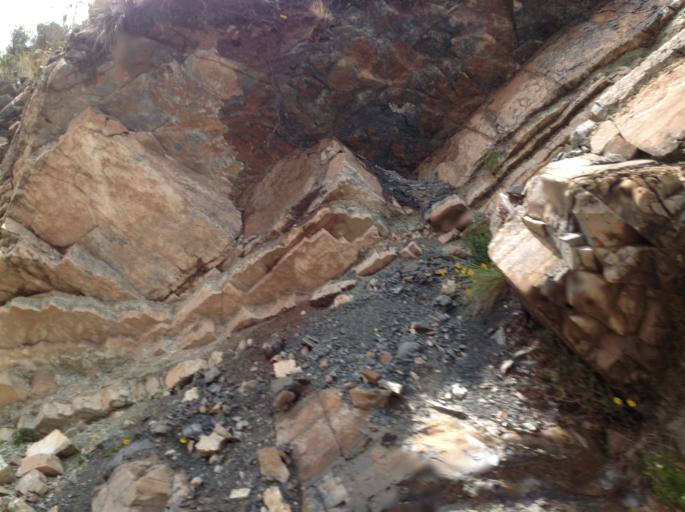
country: BO
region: La Paz
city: Yumani
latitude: -15.7745
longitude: -69.0056
